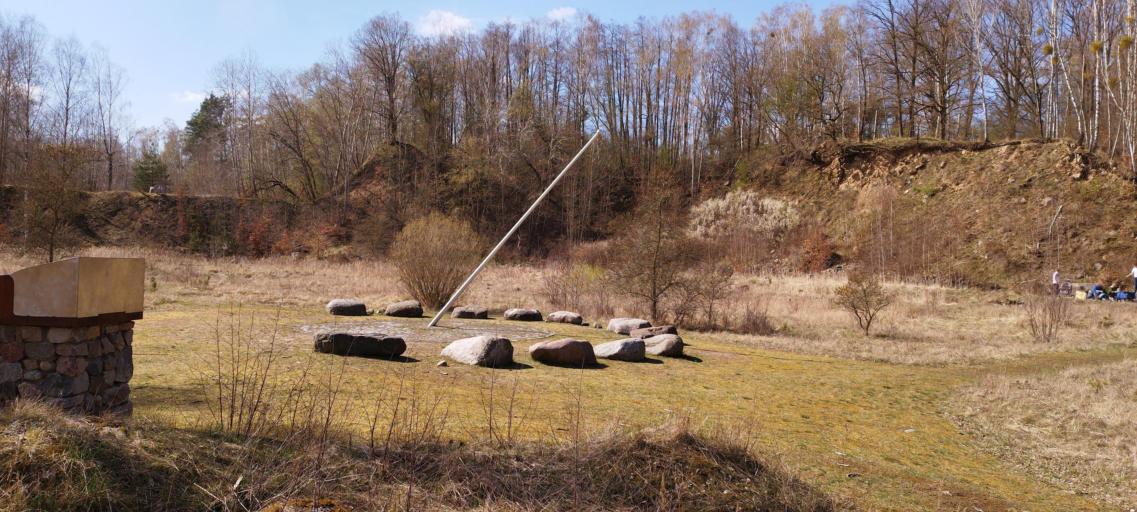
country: DE
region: Brandenburg
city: Althuttendorf
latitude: 52.9733
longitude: 13.8590
